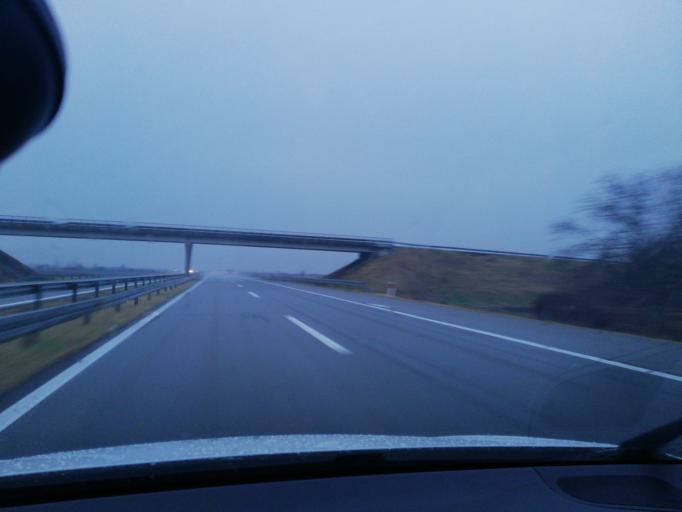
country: RS
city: Macvanska Mitrovica
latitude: 45.0132
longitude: 19.5786
